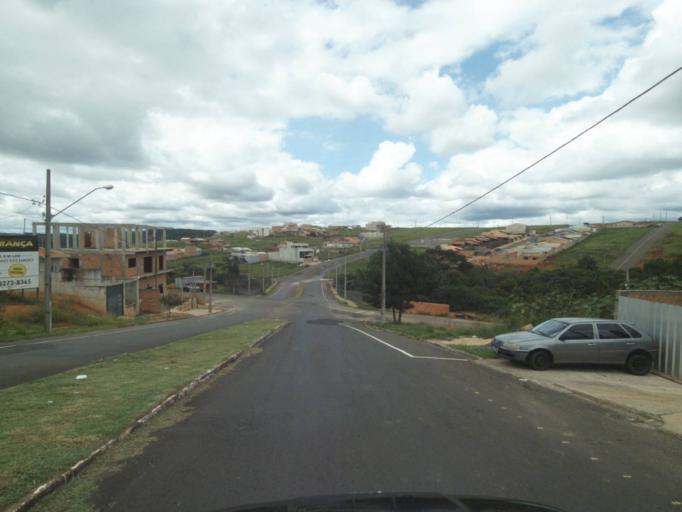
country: BR
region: Parana
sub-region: Telemaco Borba
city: Telemaco Borba
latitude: -24.3151
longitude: -50.6406
